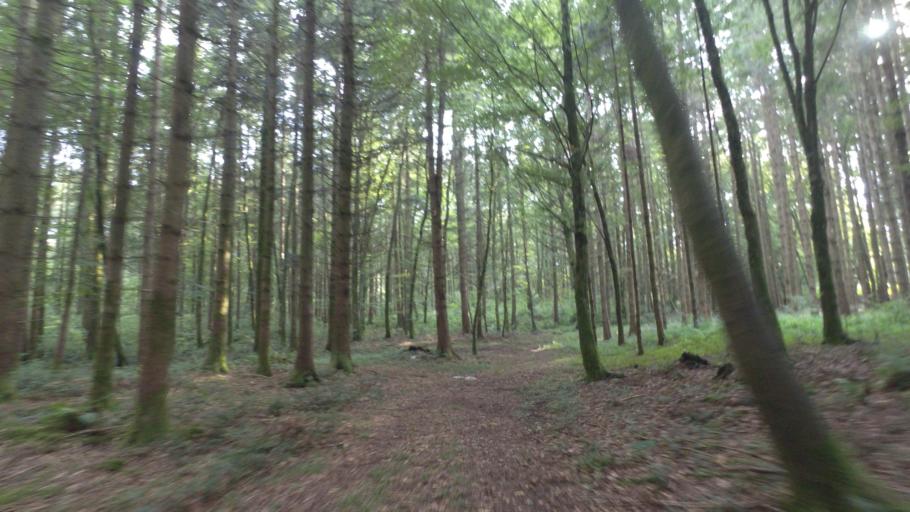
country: DE
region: Bavaria
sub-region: Upper Bavaria
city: Nussdorf
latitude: 47.9295
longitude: 12.5630
